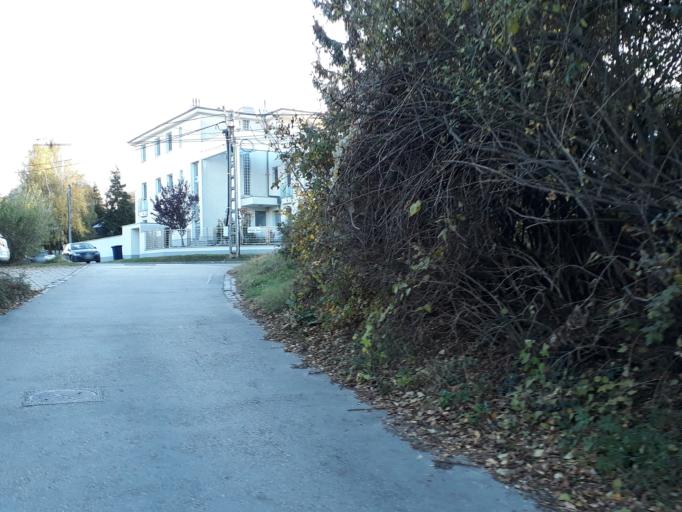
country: HU
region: Budapest
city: Budapest XII. keruelet
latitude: 47.4755
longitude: 18.9967
